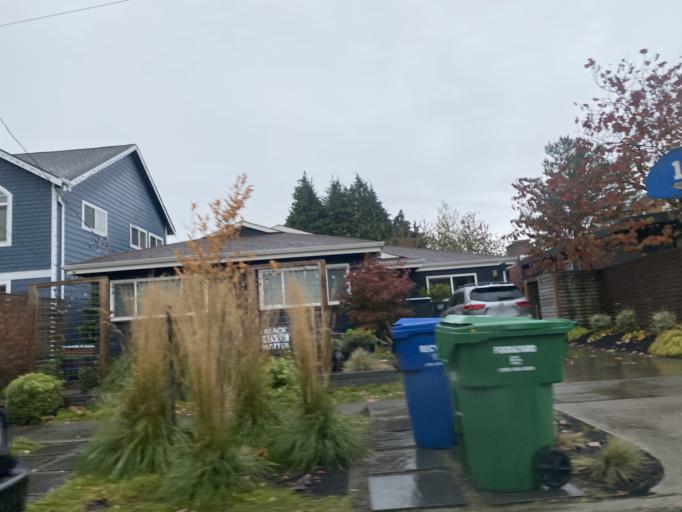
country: US
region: Washington
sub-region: King County
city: Seattle
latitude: 47.6443
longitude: -122.3890
